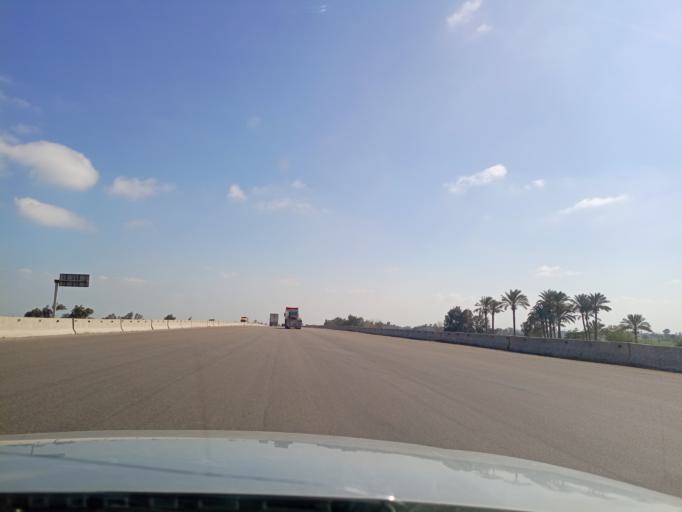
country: EG
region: Muhafazat al Qalyubiyah
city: Banha
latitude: 30.4652
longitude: 31.3047
